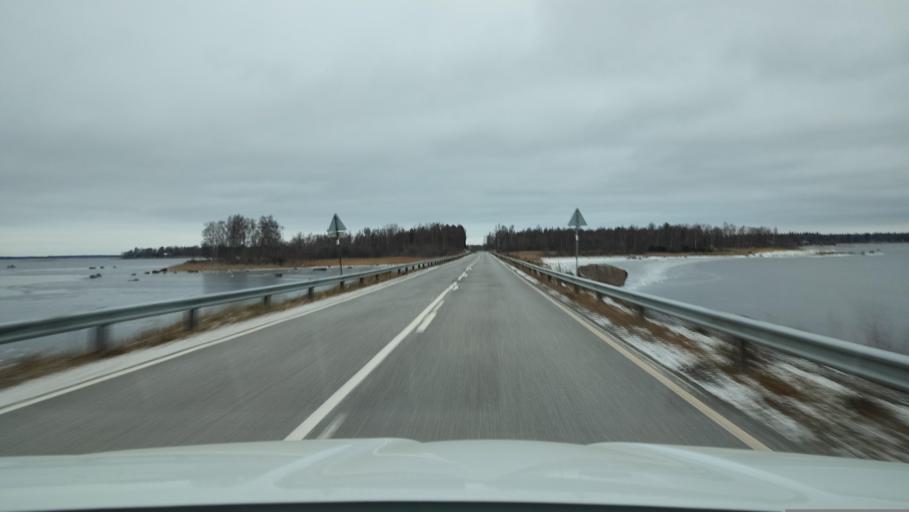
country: FI
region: Ostrobothnia
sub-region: Vaasa
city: Replot
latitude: 63.2755
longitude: 21.3432
